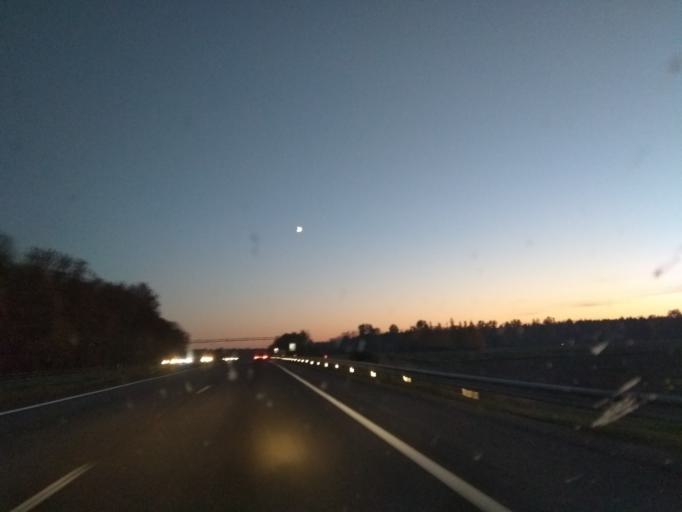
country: BY
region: Minsk
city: Enyerhyetykaw
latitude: 53.6004
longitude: 27.0442
